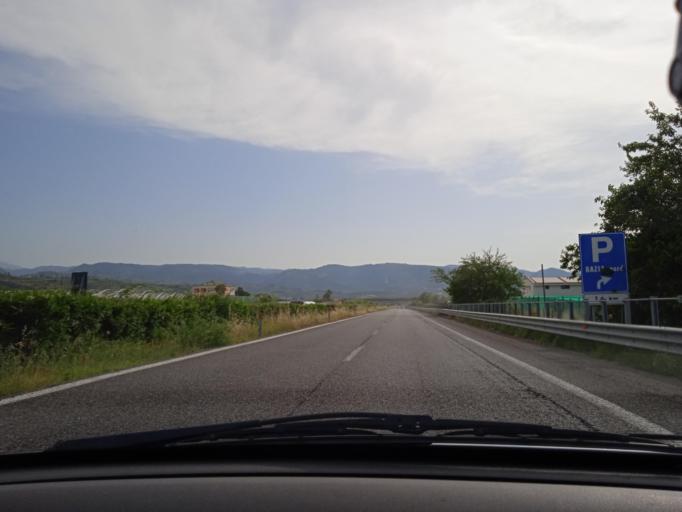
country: IT
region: Sicily
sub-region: Messina
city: Vigliatore 2
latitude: 38.1282
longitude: 15.1286
